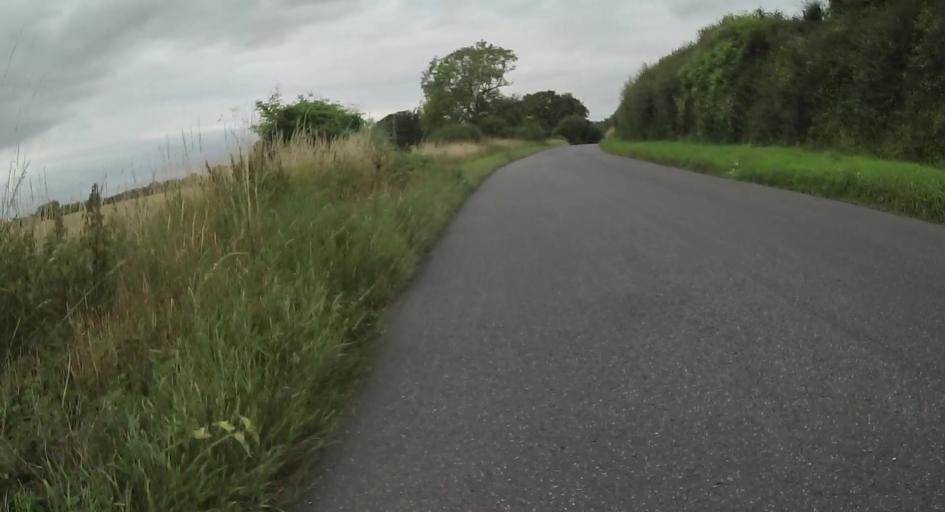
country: GB
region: England
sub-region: Hampshire
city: Bishops Waltham
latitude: 51.0208
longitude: -1.1999
